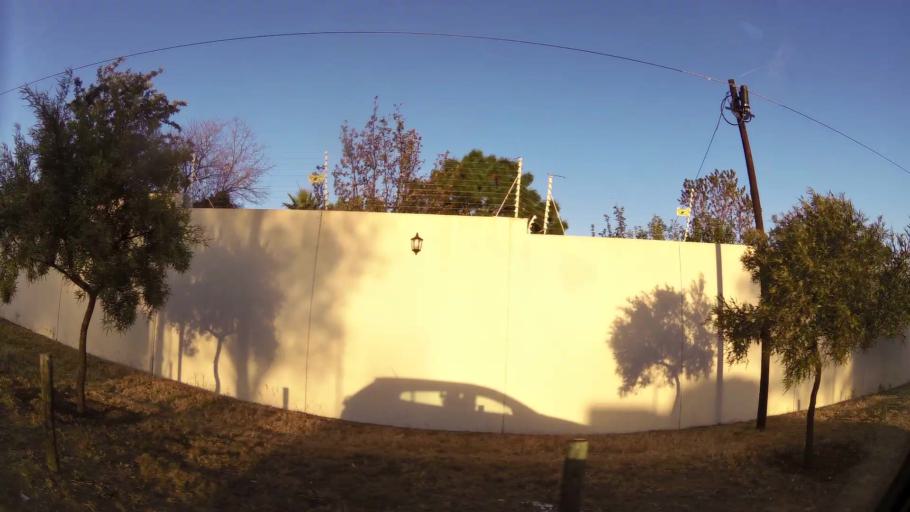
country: ZA
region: Gauteng
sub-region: City of Johannesburg Metropolitan Municipality
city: Diepsloot
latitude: -25.9476
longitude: 28.0521
